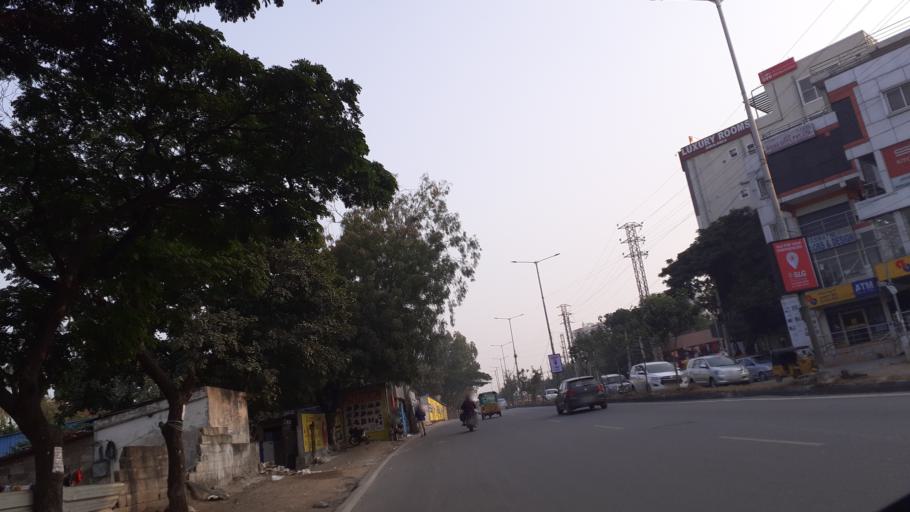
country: IN
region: Telangana
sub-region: Medak
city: Serilingampalle
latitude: 17.4915
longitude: 78.3533
